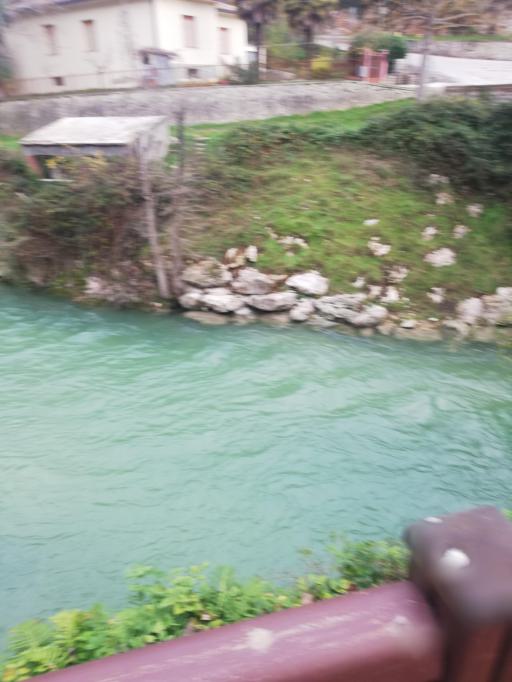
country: IT
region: The Marches
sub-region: Provincia di Ancona
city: Genga
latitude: 43.4014
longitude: 12.9696
